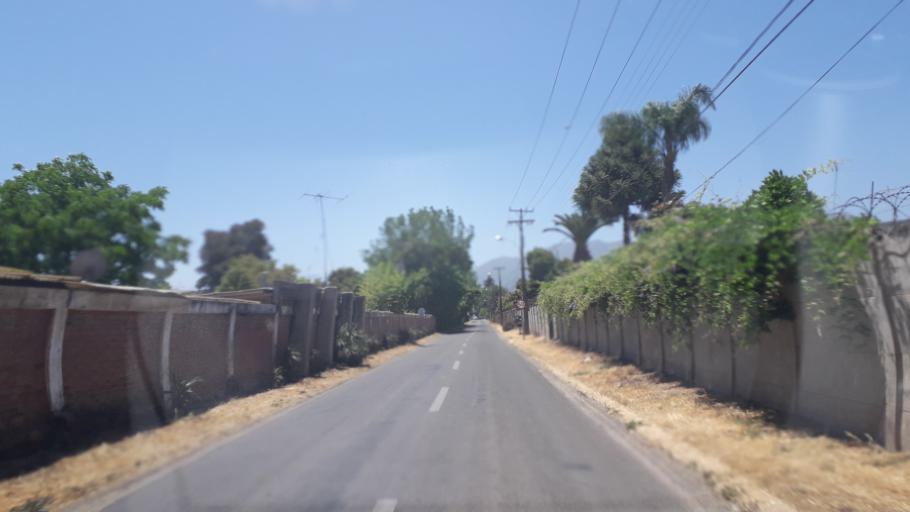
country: CL
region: Valparaiso
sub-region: Provincia de Quillota
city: Quillota
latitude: -32.9201
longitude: -71.2395
